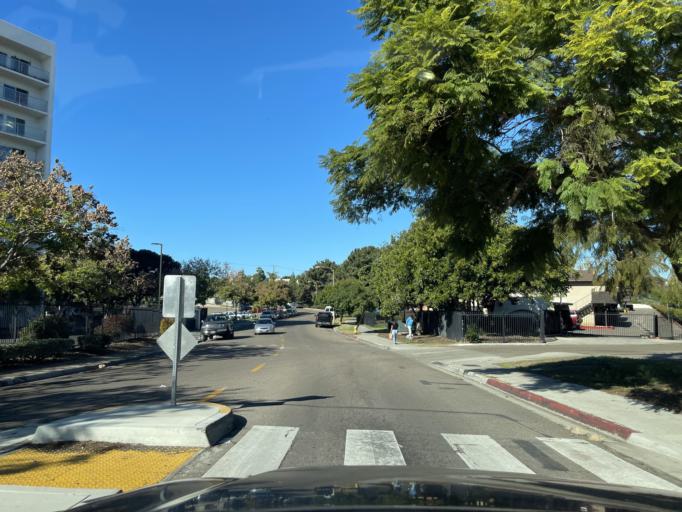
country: US
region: California
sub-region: San Diego County
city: National City
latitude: 32.6729
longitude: -117.0994
